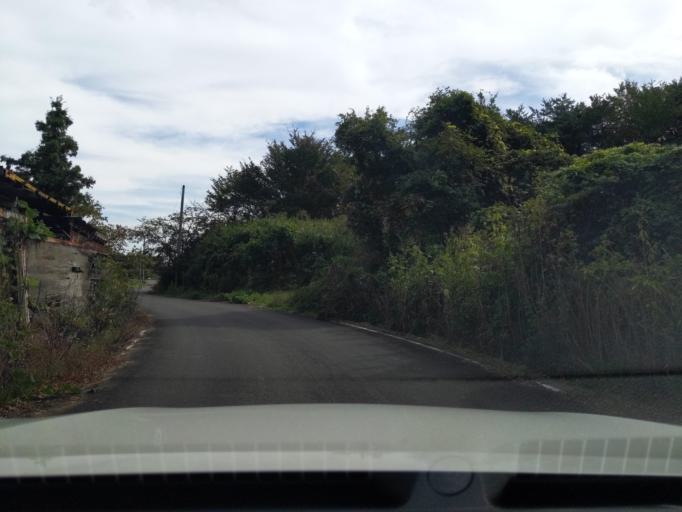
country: JP
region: Fukushima
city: Koriyama
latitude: 37.4085
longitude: 140.2777
